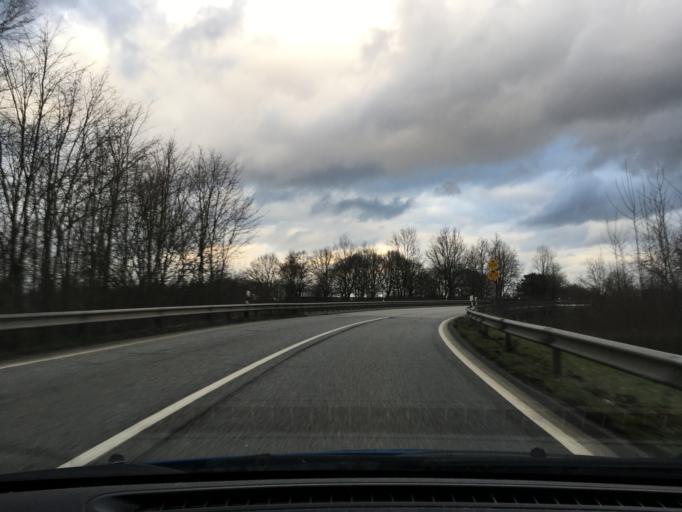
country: DE
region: Schleswig-Holstein
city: Neuenbrook
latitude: 53.8719
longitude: 9.5587
